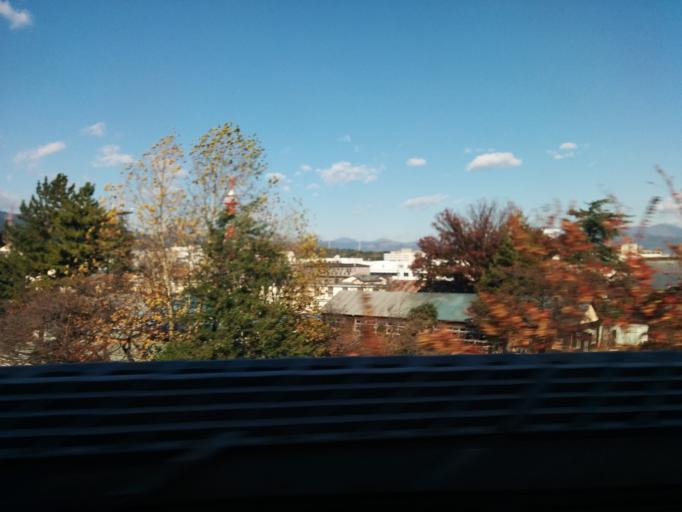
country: JP
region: Kanagawa
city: Odawara
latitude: 35.2597
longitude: 139.1579
